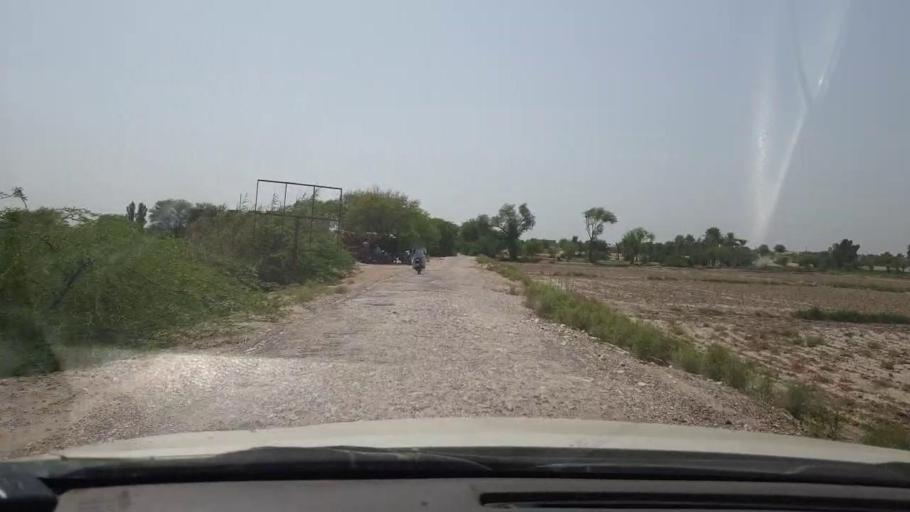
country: PK
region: Sindh
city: Rohri
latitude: 27.5212
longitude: 69.0937
